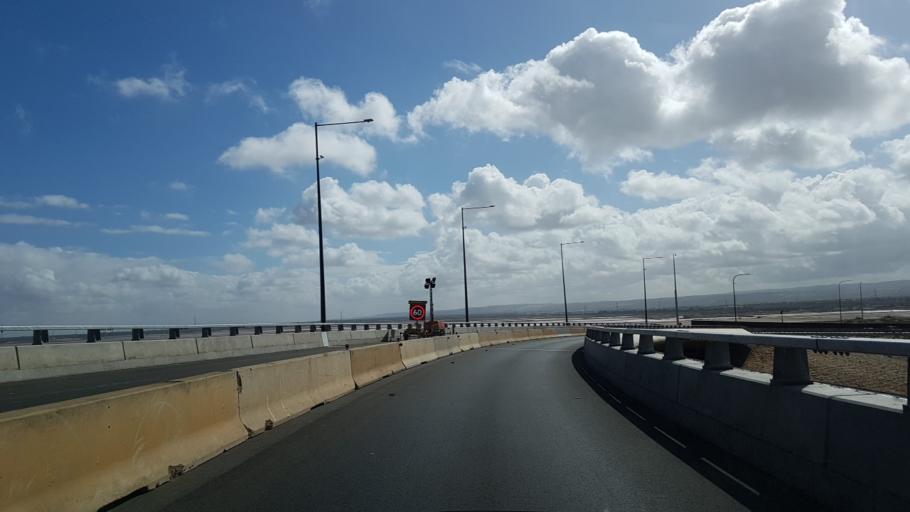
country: AU
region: South Australia
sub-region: Port Adelaide Enfield
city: Blair Athol
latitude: -34.8293
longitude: 138.5627
